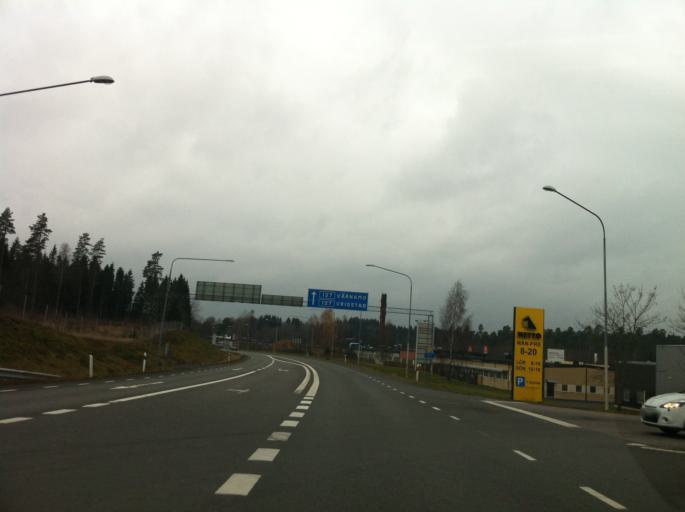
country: SE
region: Joenkoeping
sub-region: Savsjo Kommun
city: Saevsjoe
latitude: 57.3943
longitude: 14.6874
